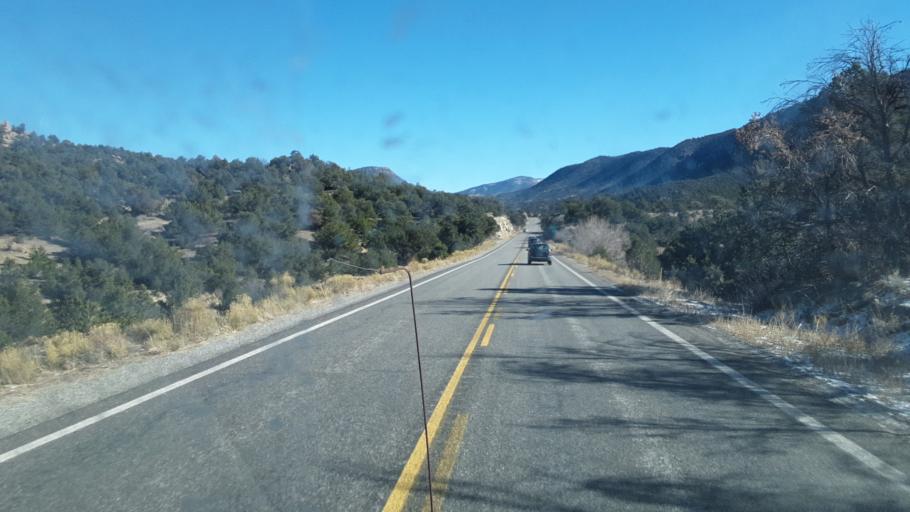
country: US
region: Colorado
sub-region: Chaffee County
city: Buena Vista
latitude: 38.8183
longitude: -106.0726
